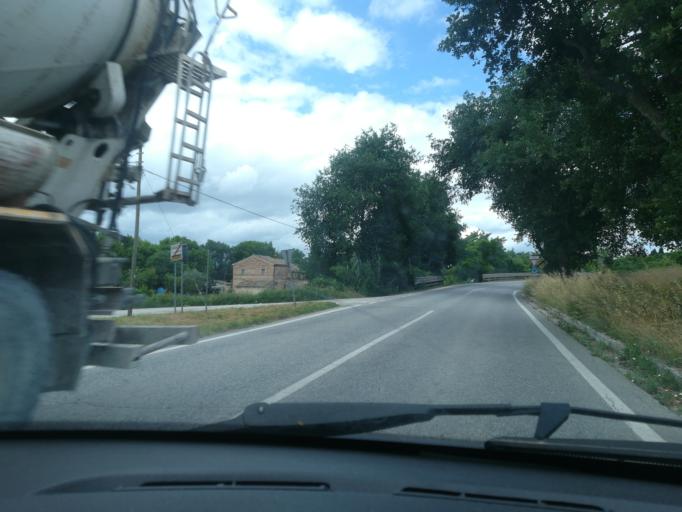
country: IT
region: The Marches
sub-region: Provincia di Macerata
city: Sforzacosta
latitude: 43.2595
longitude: 13.4255
